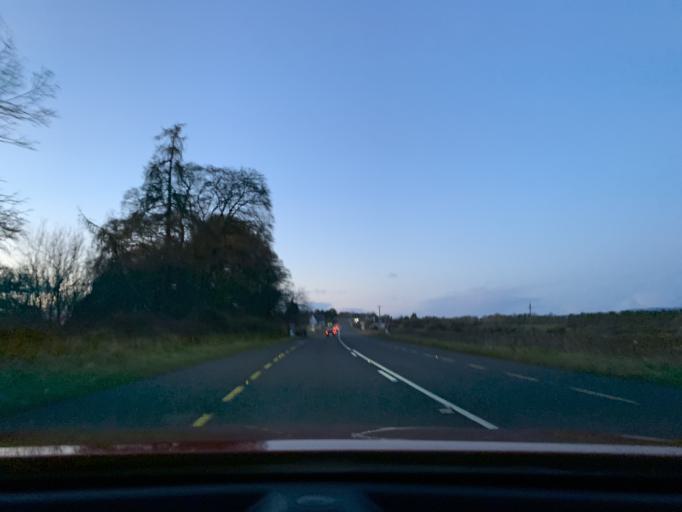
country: IE
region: Connaught
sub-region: County Leitrim
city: Carrick-on-Shannon
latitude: 53.9626
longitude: -8.1938
